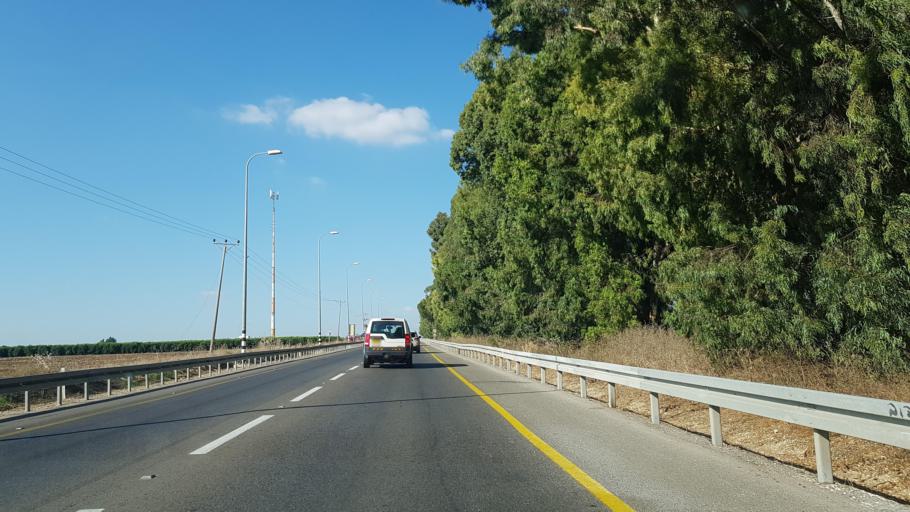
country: PS
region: West Bank
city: Tulkarm
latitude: 32.3166
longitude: 34.9993
